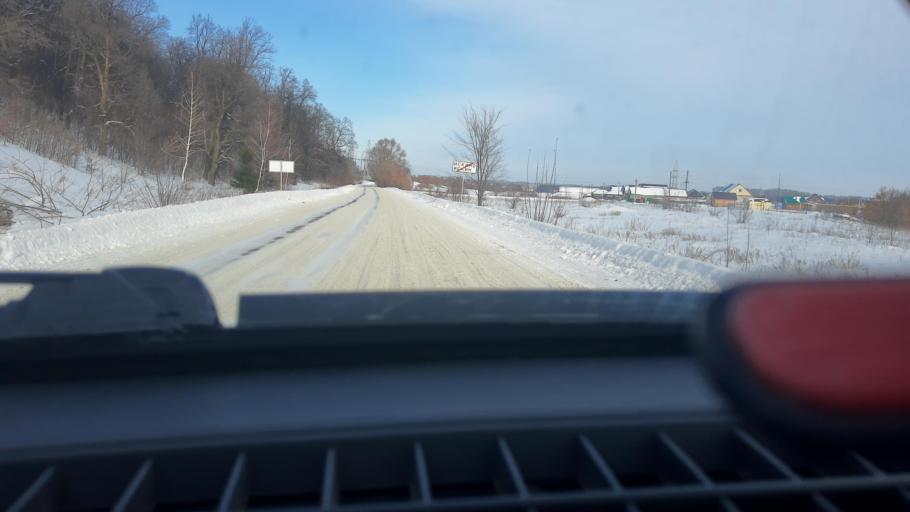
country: RU
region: Bashkortostan
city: Ufa
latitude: 54.5274
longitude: 55.9109
